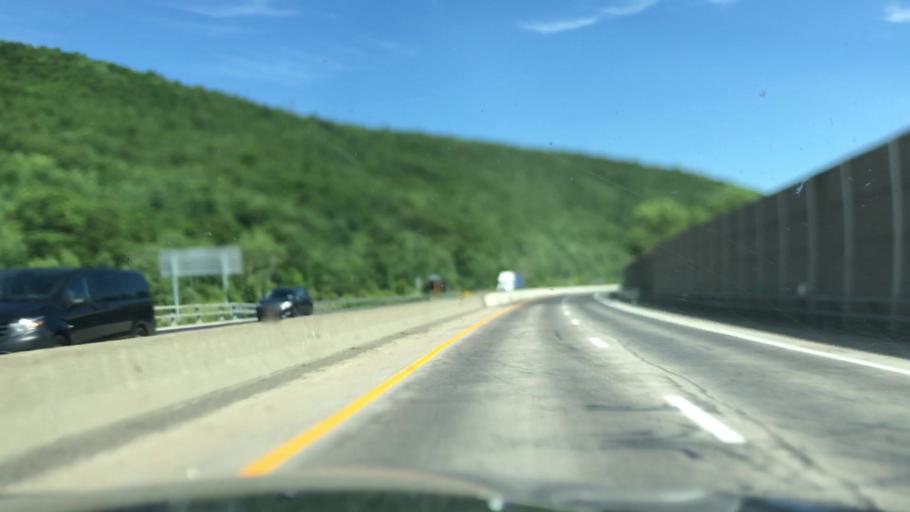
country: US
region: New York
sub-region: Steuben County
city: Corning
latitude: 42.1523
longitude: -77.0451
